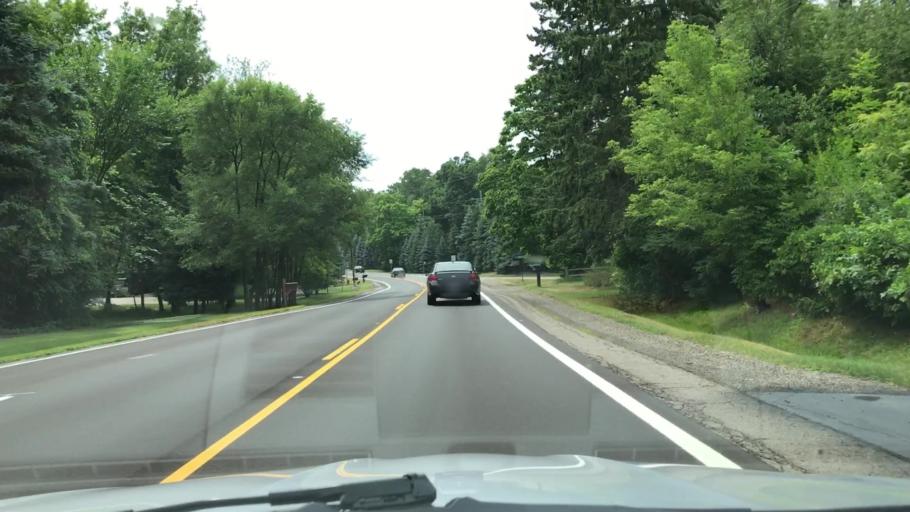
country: US
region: Michigan
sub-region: Oakland County
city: West Bloomfield Township
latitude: 42.5711
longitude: -83.3975
